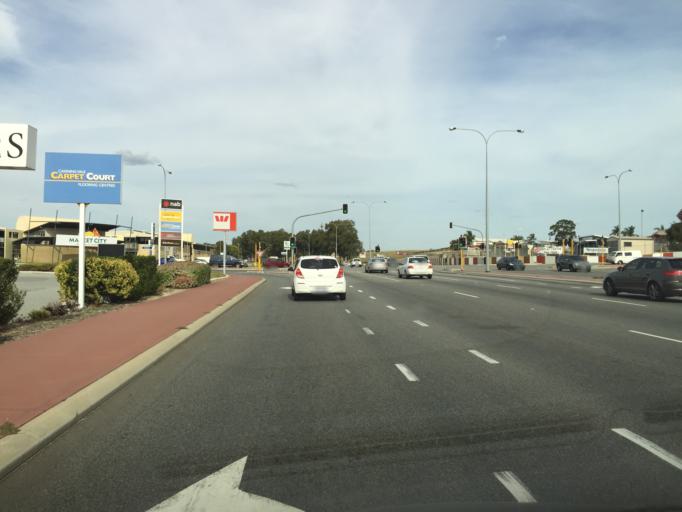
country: AU
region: Western Australia
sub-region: Canning
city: Willetton
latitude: -32.0714
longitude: 115.8924
